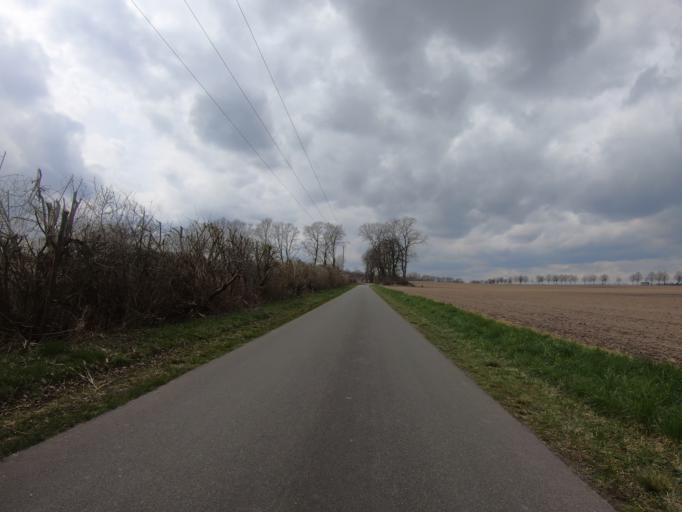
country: DE
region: Lower Saxony
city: Hankensbuttel
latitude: 52.7286
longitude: 10.6363
